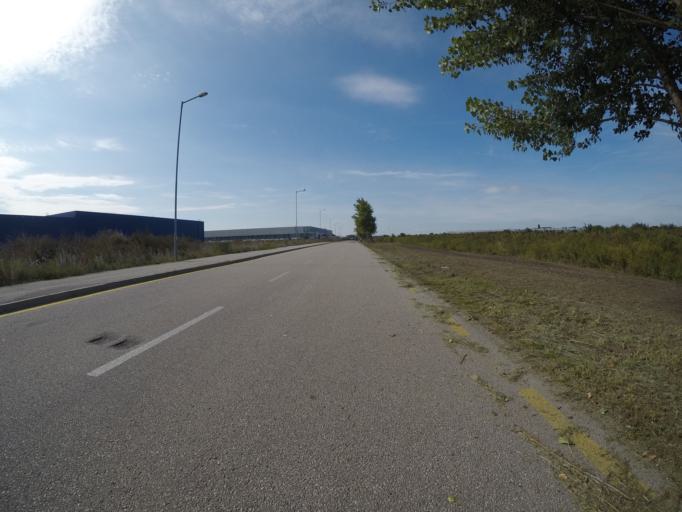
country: SK
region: Trnavsky
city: Dunajska Streda
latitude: 47.9859
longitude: 17.6250
